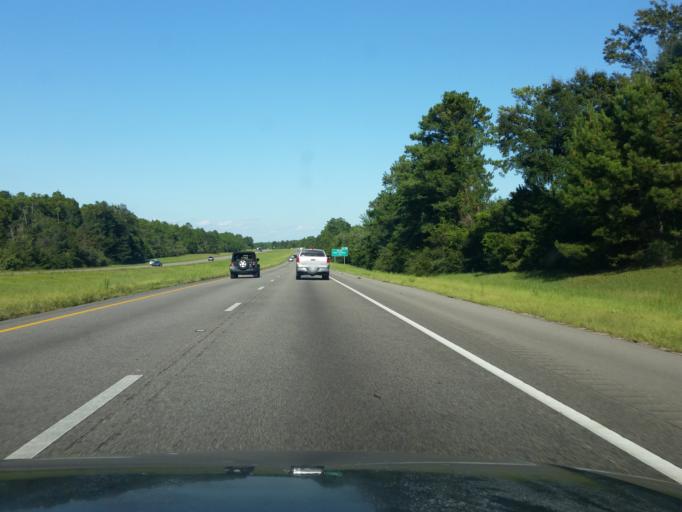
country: US
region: Mississippi
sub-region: Hancock County
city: Diamondhead
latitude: 30.3855
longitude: -89.3344
